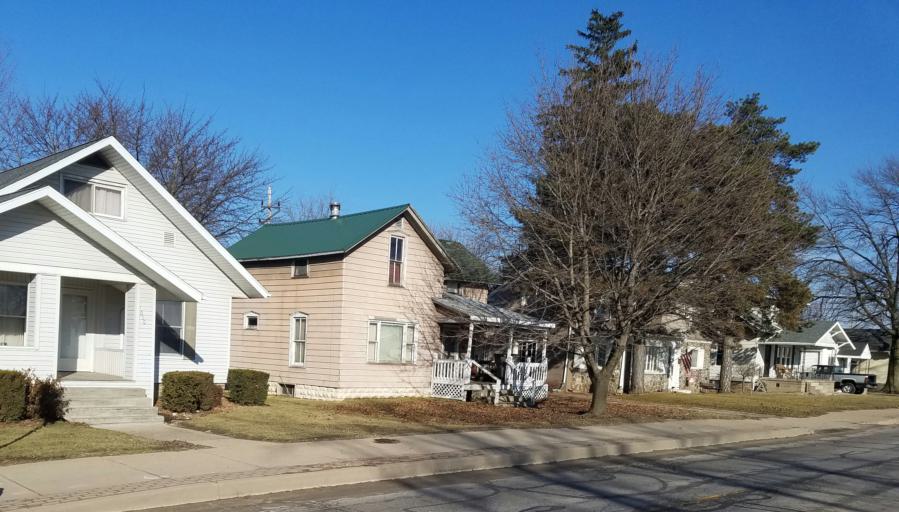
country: US
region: Indiana
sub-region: Elkhart County
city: Nappanee
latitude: 41.4427
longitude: -85.9943
